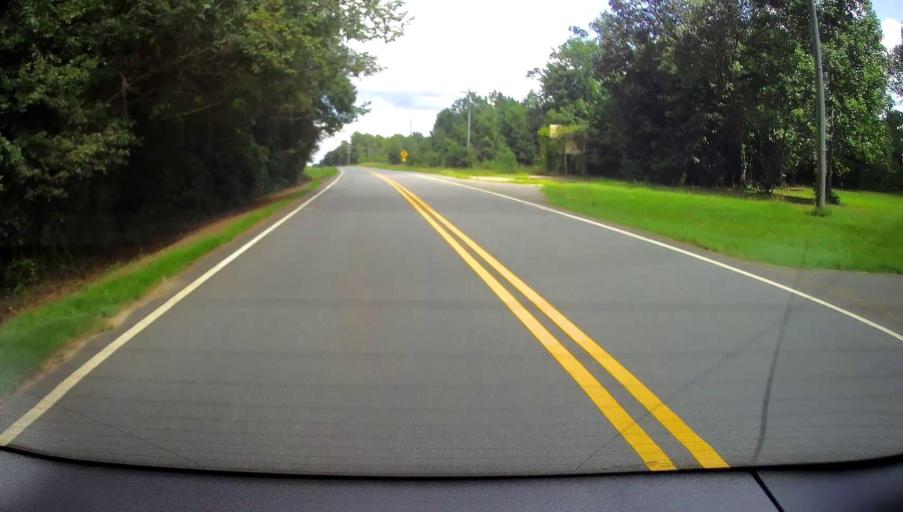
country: US
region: Georgia
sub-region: Bibb County
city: West Point
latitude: 32.8650
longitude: -83.8814
